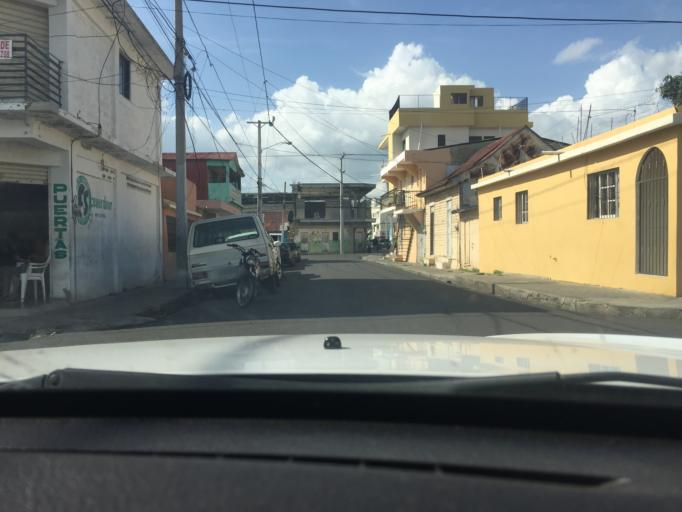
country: DO
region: Santiago
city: Santiago de los Caballeros
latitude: 19.4543
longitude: -70.7115
